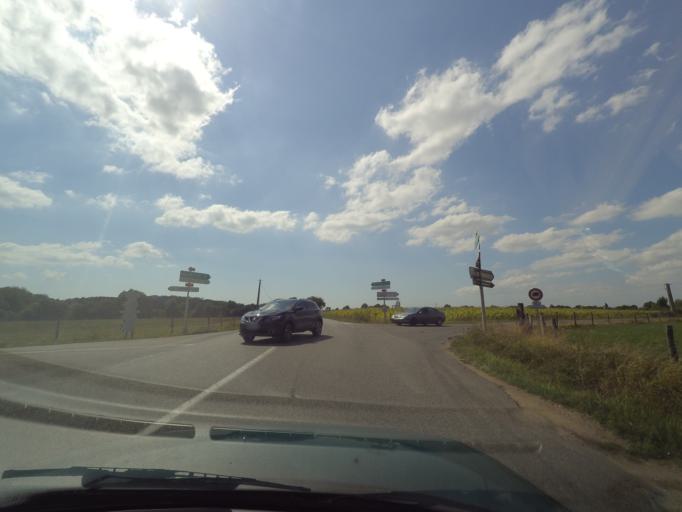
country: FR
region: Pays de la Loire
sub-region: Departement de la Loire-Atlantique
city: Sainte-Pazanne
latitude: 47.0970
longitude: -1.8213
